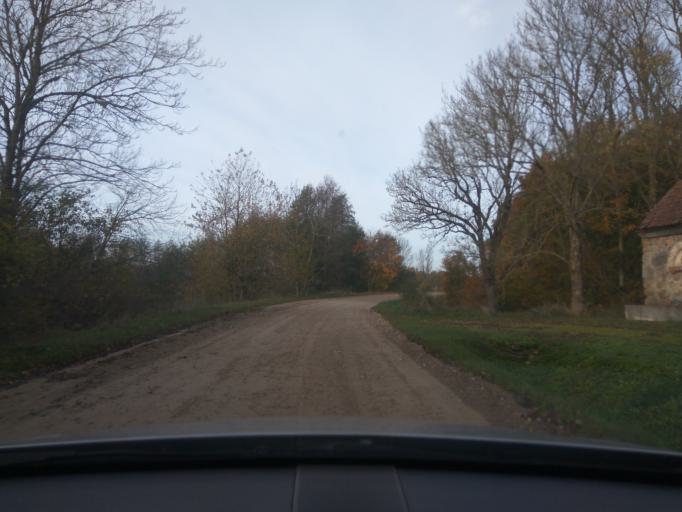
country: LV
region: Alsunga
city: Alsunga
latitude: 56.8755
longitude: 21.6788
